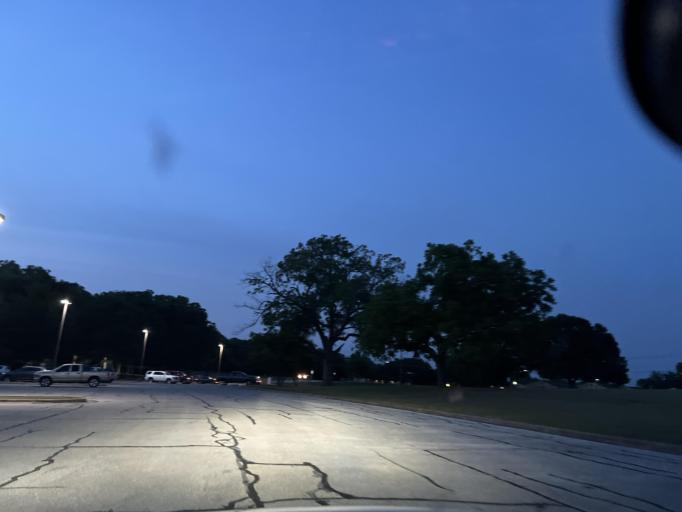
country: US
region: Texas
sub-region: Washington County
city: Brenham
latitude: 30.1847
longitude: -96.4053
